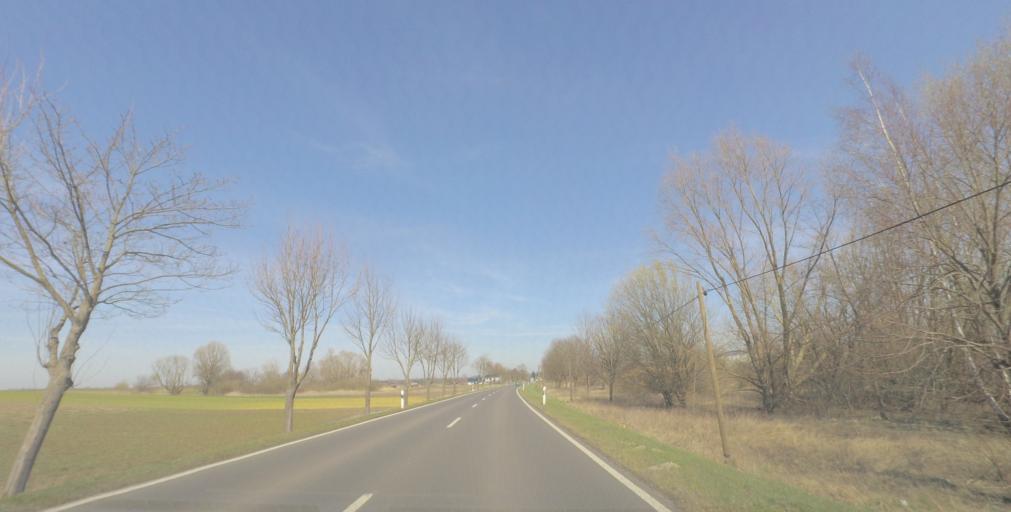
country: DE
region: Brandenburg
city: Neuruppin
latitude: 52.8779
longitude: 12.7896
